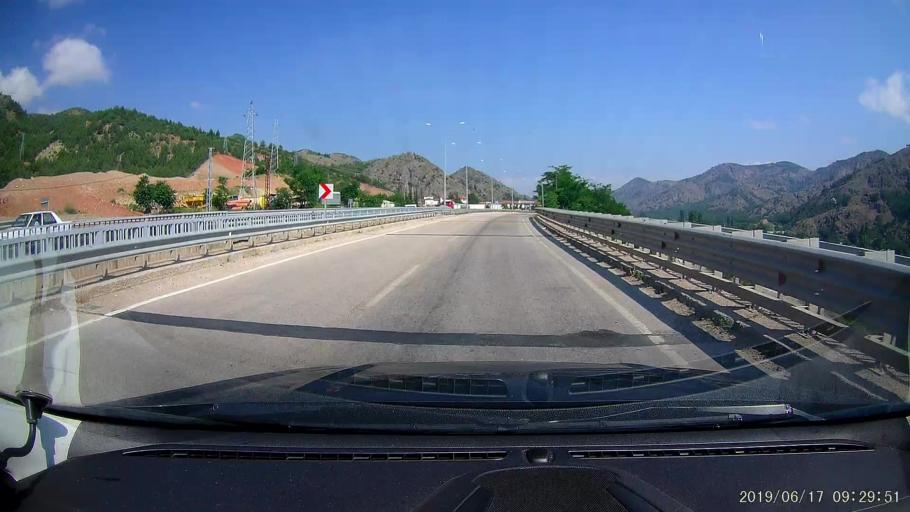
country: TR
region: Amasya
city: Amasya
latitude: 40.6998
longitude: 35.8073
